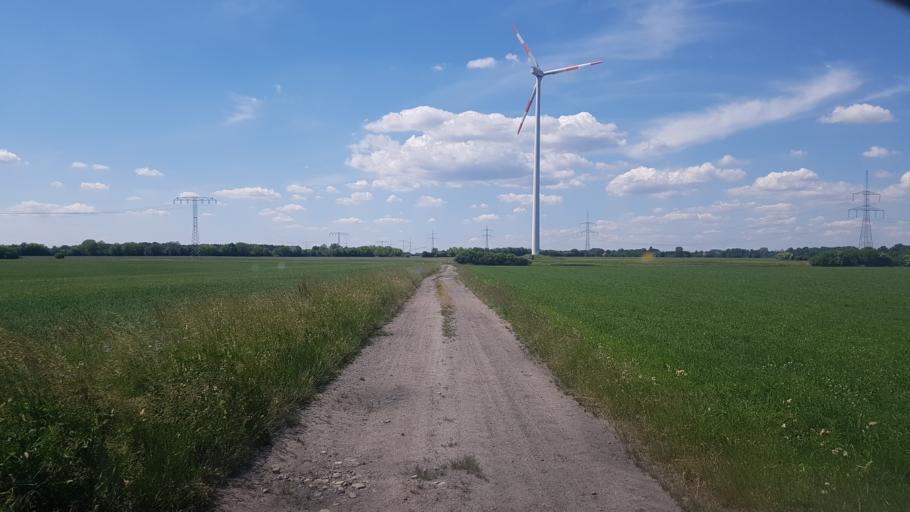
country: DE
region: Brandenburg
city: Finsterwalde
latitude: 51.6491
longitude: 13.7315
